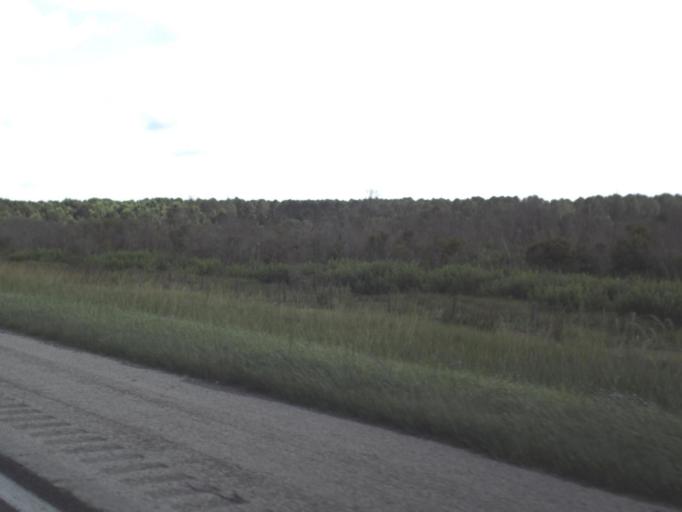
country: US
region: Florida
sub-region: Alachua County
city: Gainesville
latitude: 29.5838
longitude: -82.3587
